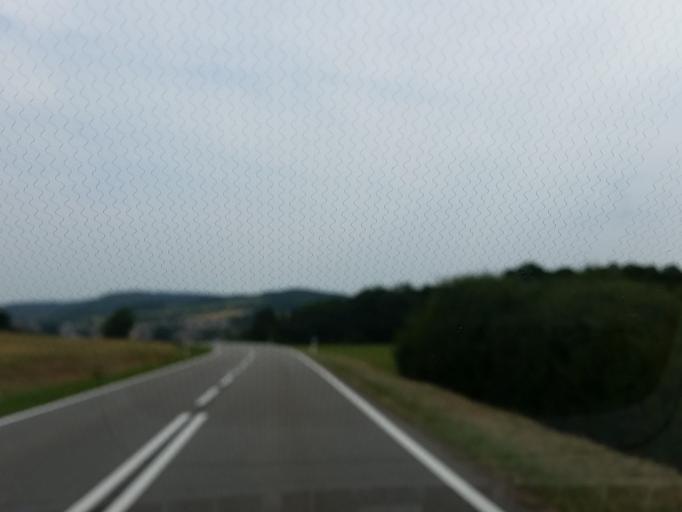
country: DE
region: Saarland
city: Wadern
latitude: 49.5562
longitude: 6.9150
